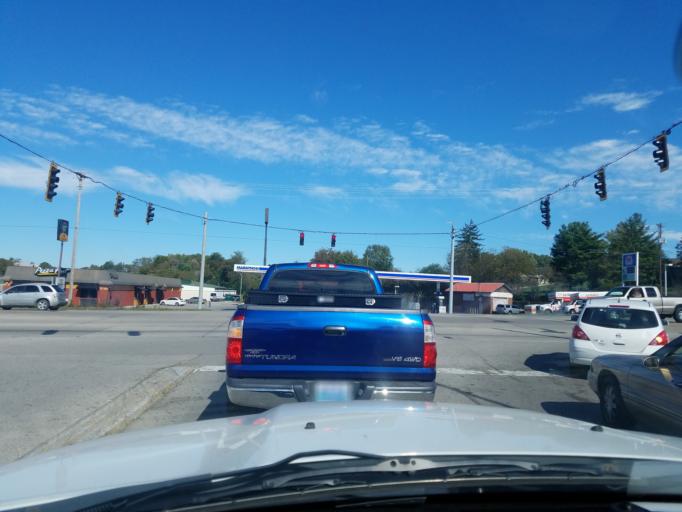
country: US
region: Kentucky
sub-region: Laurel County
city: London
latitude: 37.1085
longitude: -84.0889
